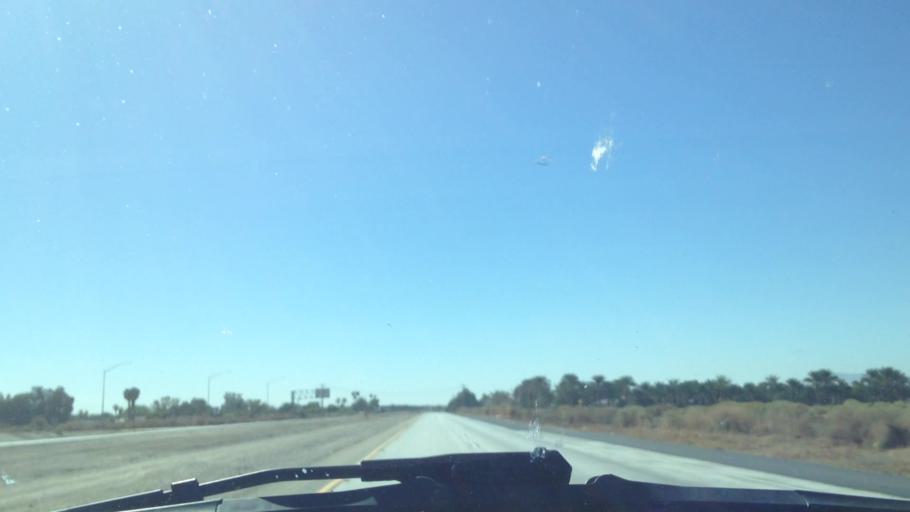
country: US
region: California
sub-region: Riverside County
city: Thermal
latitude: 33.6411
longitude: -116.1324
